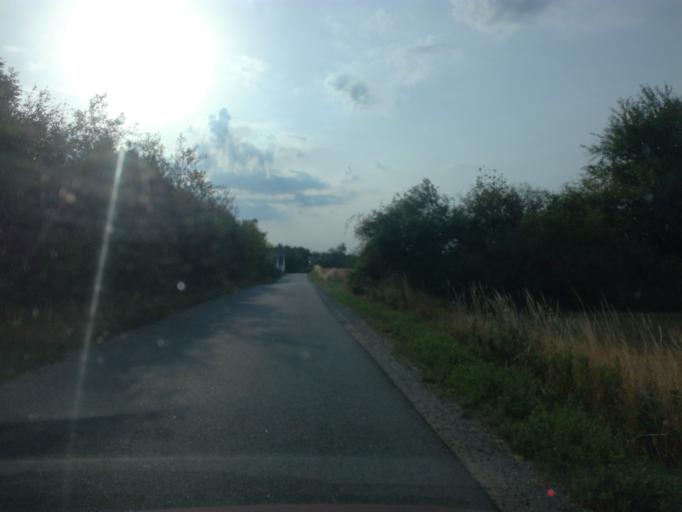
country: DK
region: South Denmark
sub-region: Vejle Kommune
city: Vejle
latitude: 55.6477
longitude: 9.5712
